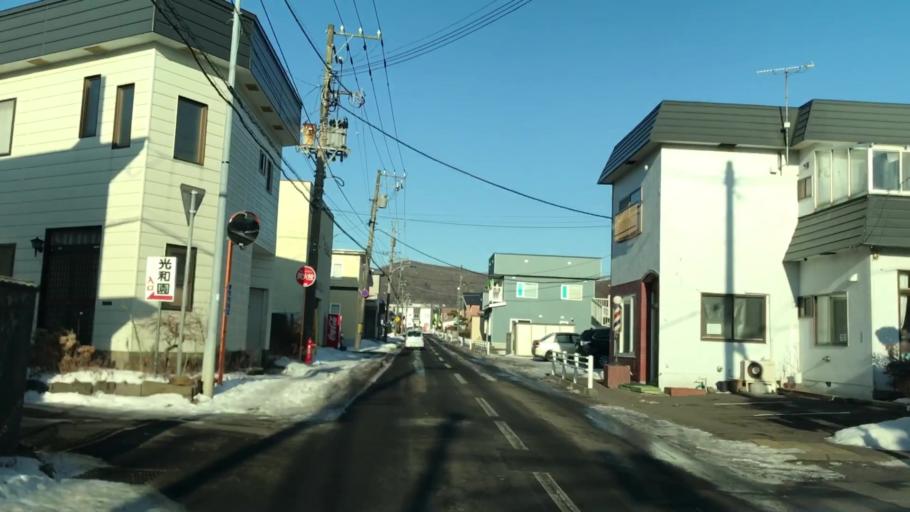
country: JP
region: Hokkaido
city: Muroran
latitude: 42.3644
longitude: 141.0437
